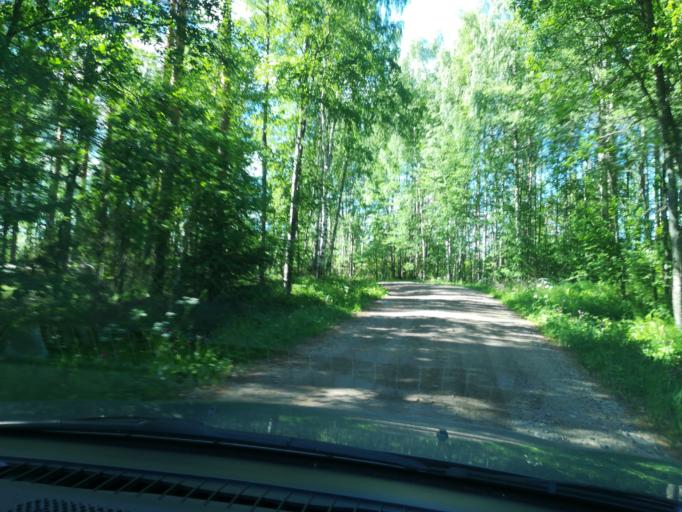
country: FI
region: Southern Savonia
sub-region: Mikkeli
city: Puumala
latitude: 61.6613
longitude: 28.1521
